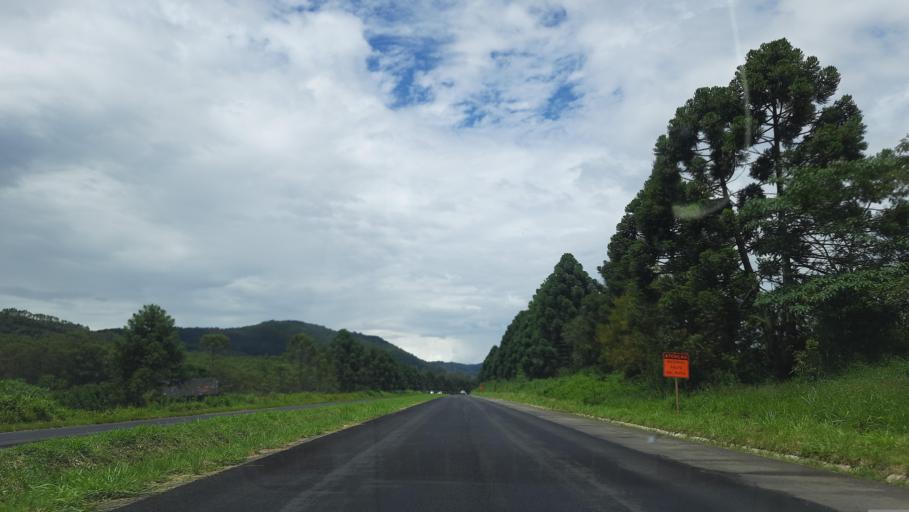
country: BR
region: Minas Gerais
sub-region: Pocos De Caldas
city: Pocos de Caldas
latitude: -21.8156
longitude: -46.6609
